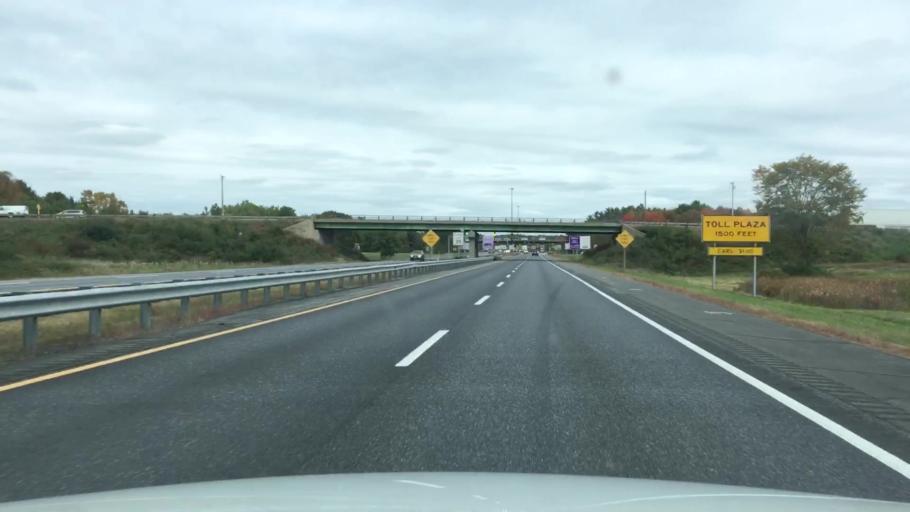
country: US
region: Maine
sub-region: Kennebec County
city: Gardiner
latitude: 44.2081
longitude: -69.8247
